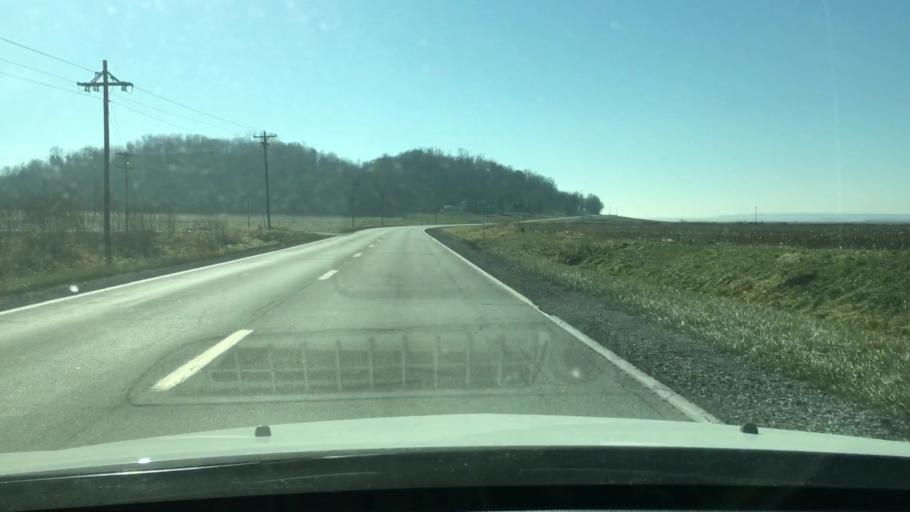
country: US
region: Illinois
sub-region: Morgan County
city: Meredosia
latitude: 39.7067
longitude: -90.5685
